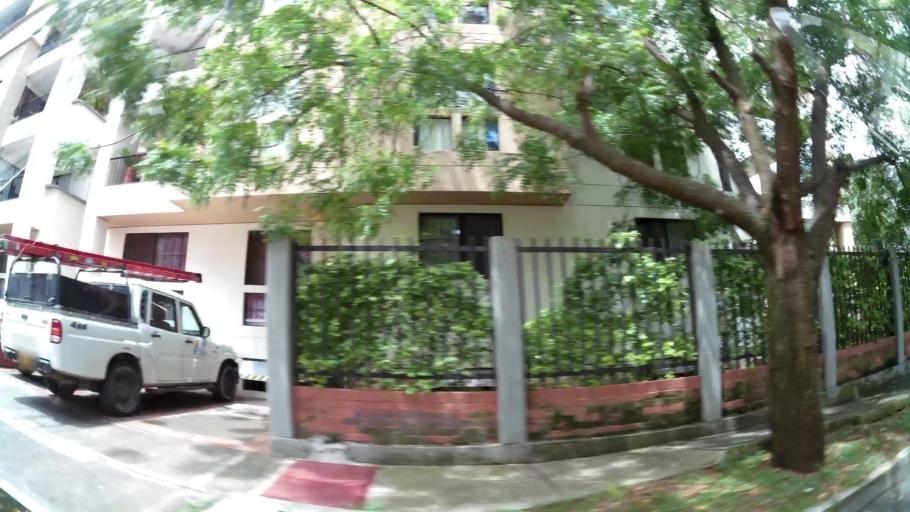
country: CO
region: Valle del Cauca
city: Cali
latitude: 3.3826
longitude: -76.5351
